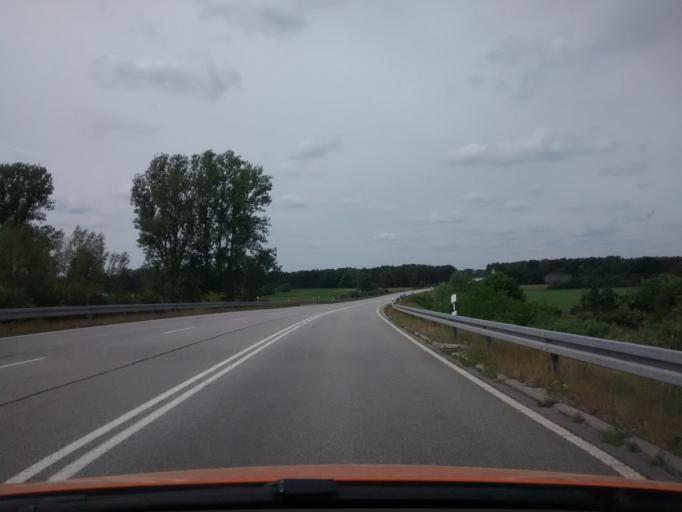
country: DE
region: Brandenburg
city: Luckenwalde
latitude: 52.1232
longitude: 13.2028
